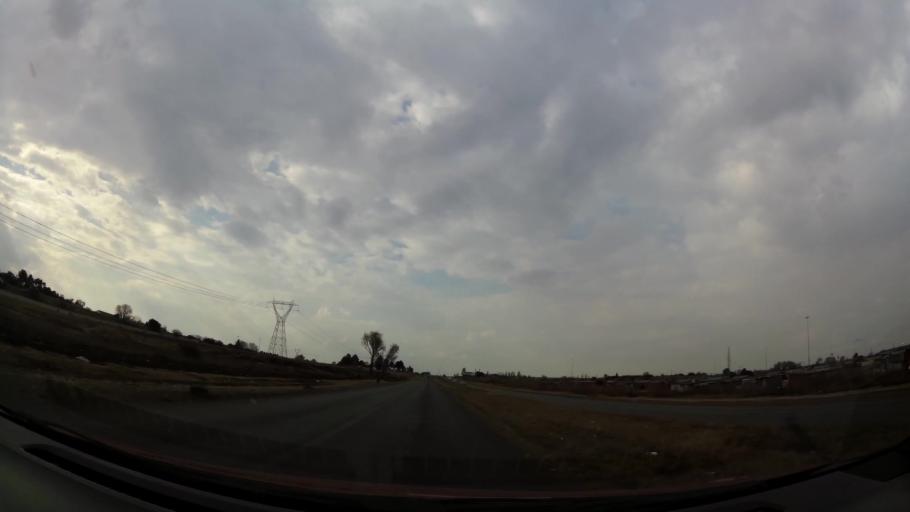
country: ZA
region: Gauteng
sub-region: Sedibeng District Municipality
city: Vanderbijlpark
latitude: -26.6647
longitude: 27.8416
